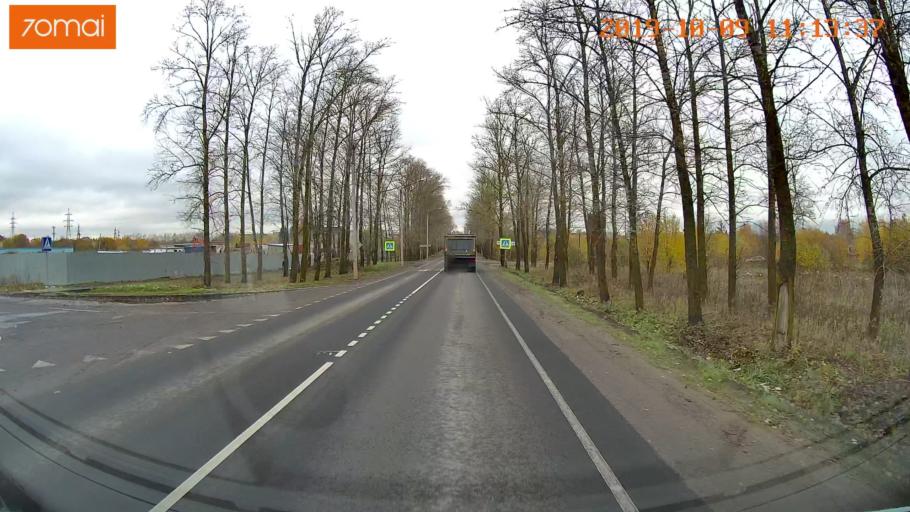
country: RU
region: Vologda
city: Vologda
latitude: 59.1831
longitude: 39.8451
